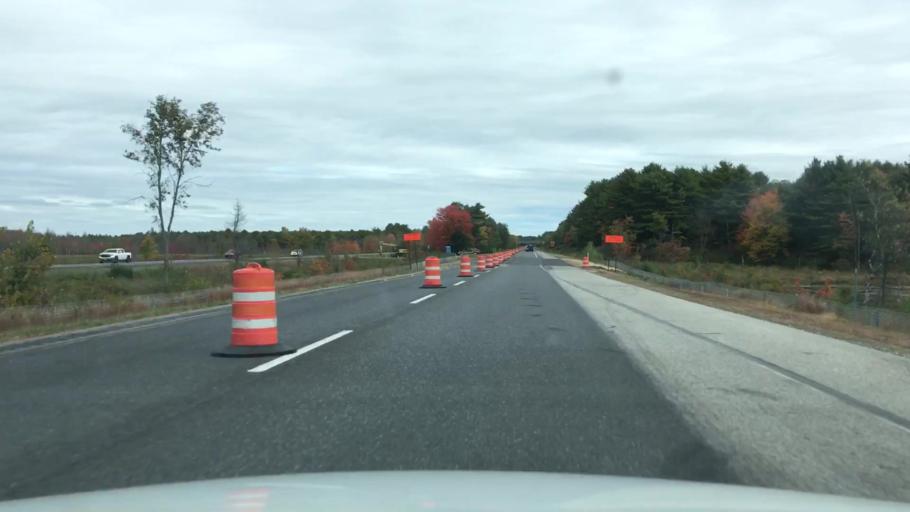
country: US
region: Maine
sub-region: Sagadahoc County
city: Richmond
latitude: 44.1058
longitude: -69.8643
